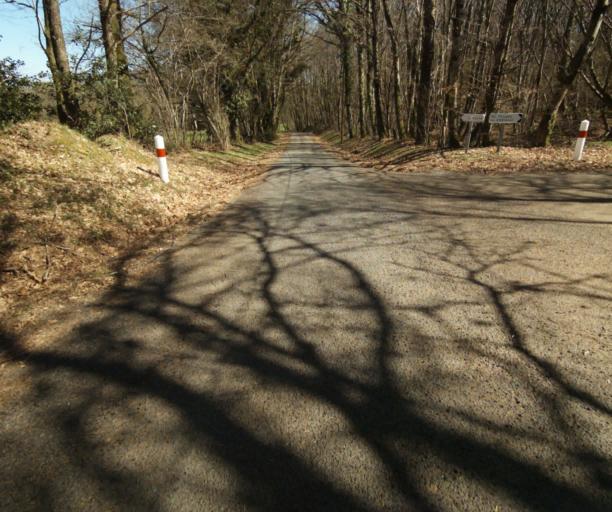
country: FR
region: Limousin
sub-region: Departement de la Correze
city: Chamboulive
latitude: 45.4005
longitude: 1.6652
